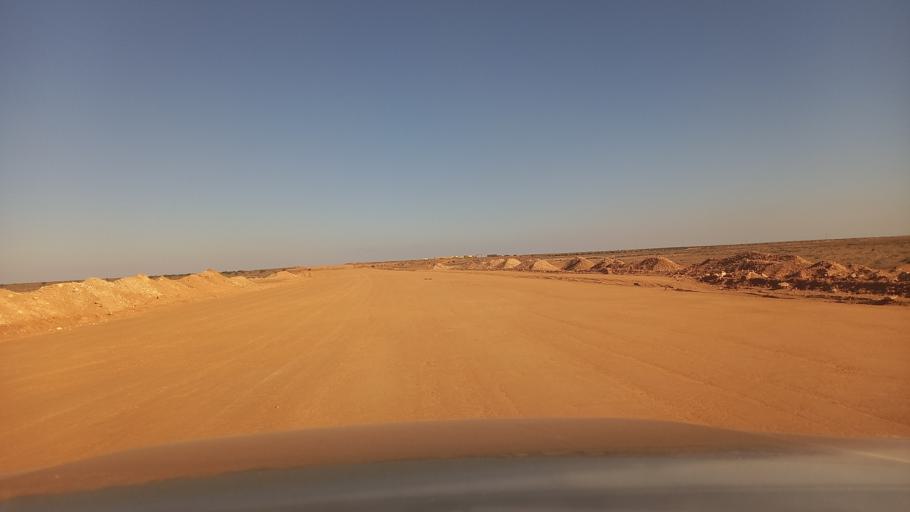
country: TN
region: Madanin
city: Medenine
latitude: 33.1691
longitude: 10.5253
